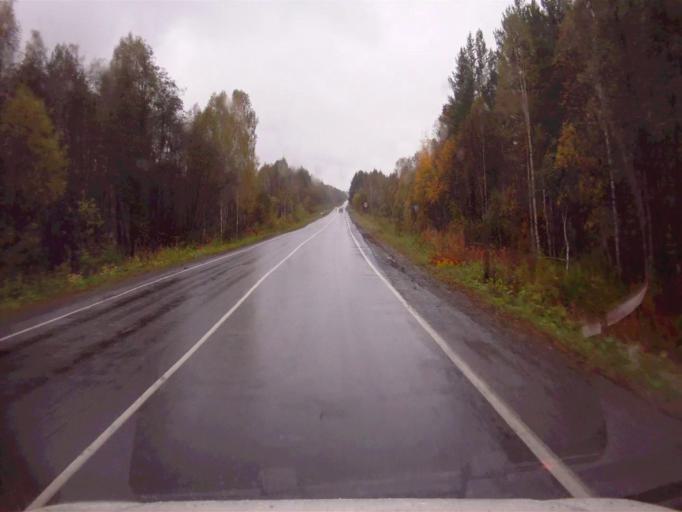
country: RU
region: Chelyabinsk
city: Verkhniy Ufaley
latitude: 55.9718
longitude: 60.3566
